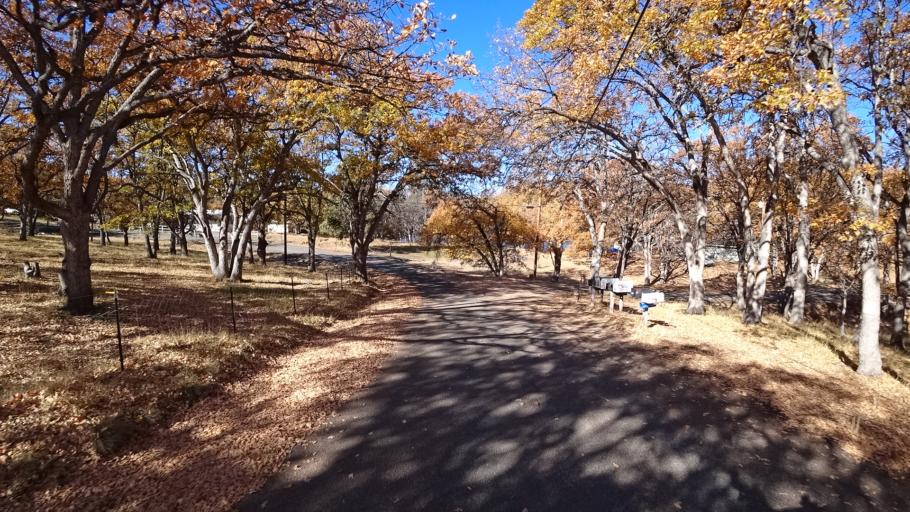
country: US
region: California
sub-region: Siskiyou County
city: Montague
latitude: 41.9788
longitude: -122.3250
